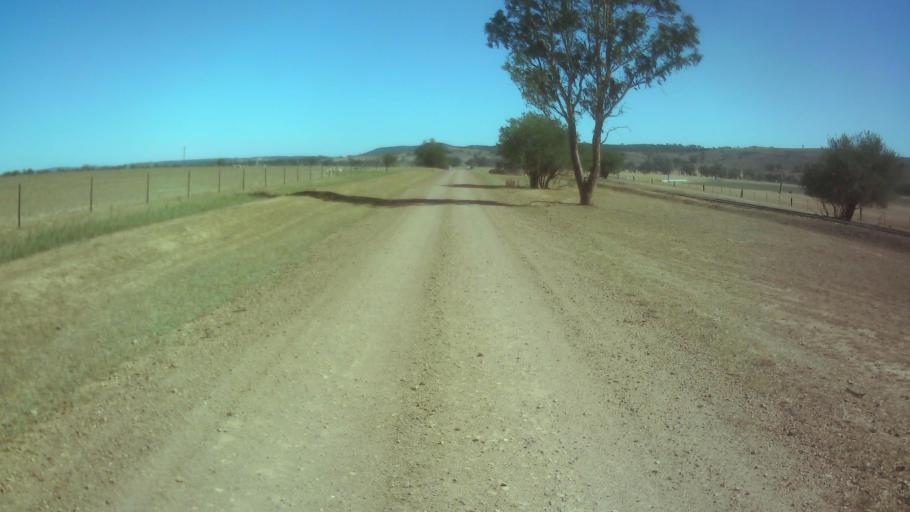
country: AU
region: New South Wales
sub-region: Weddin
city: Grenfell
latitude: -33.9566
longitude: 148.3025
